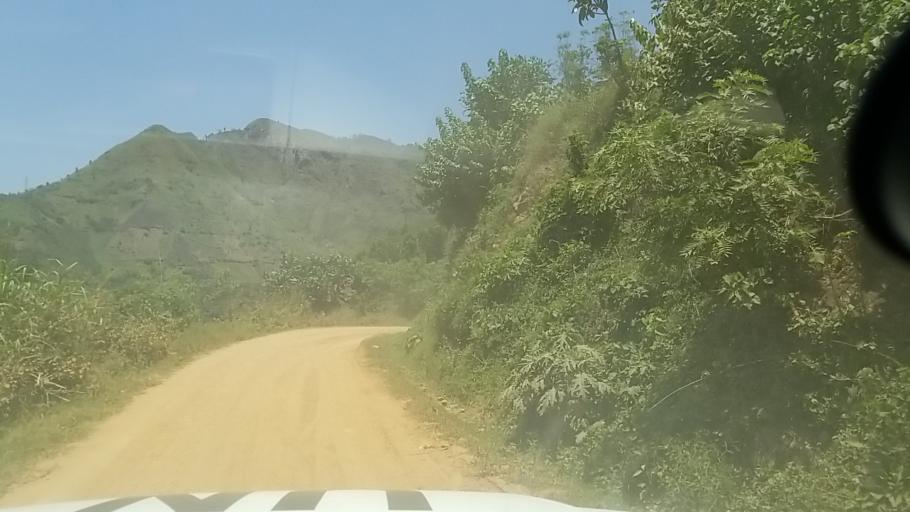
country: CD
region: Nord Kivu
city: Sake
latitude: -1.8396
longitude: 28.9985
